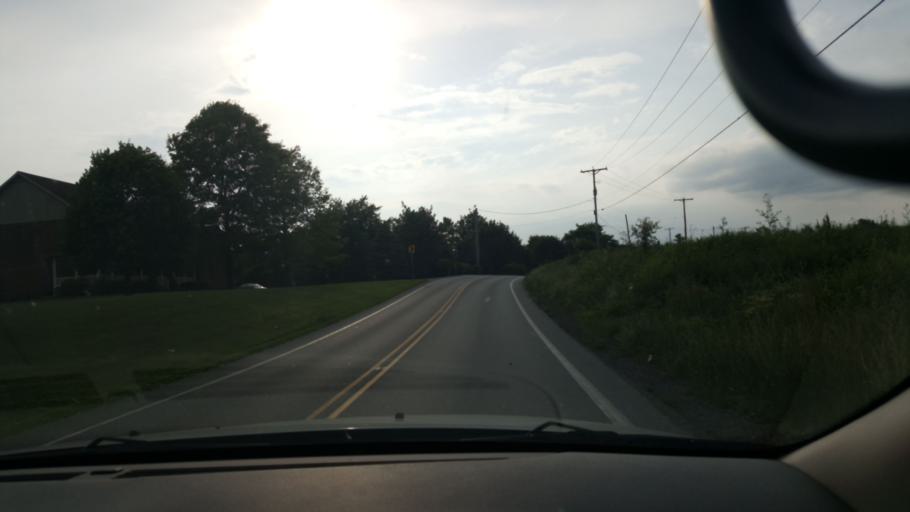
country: US
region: Pennsylvania
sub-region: York County
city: Shiloh
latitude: 39.9910
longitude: -76.7908
